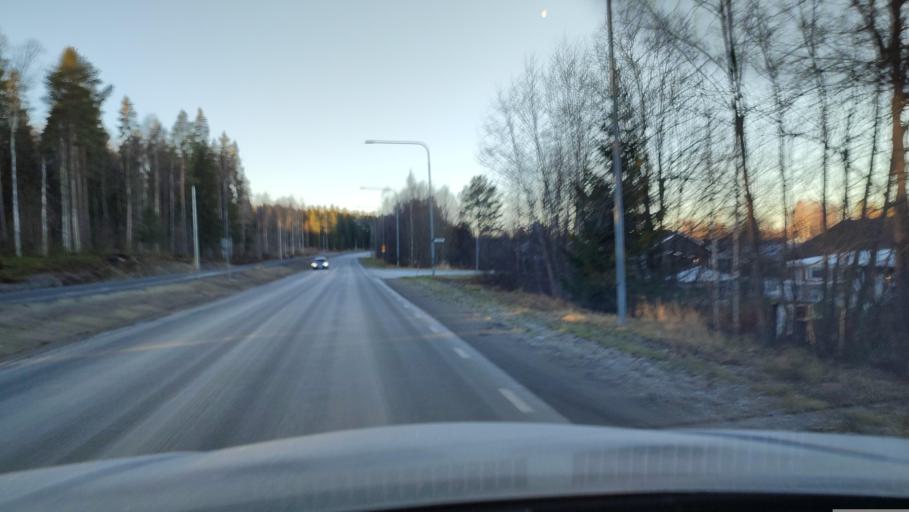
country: SE
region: Vaesterbotten
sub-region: Skelleftea Kommun
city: Viken
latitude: 64.7398
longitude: 20.9319
